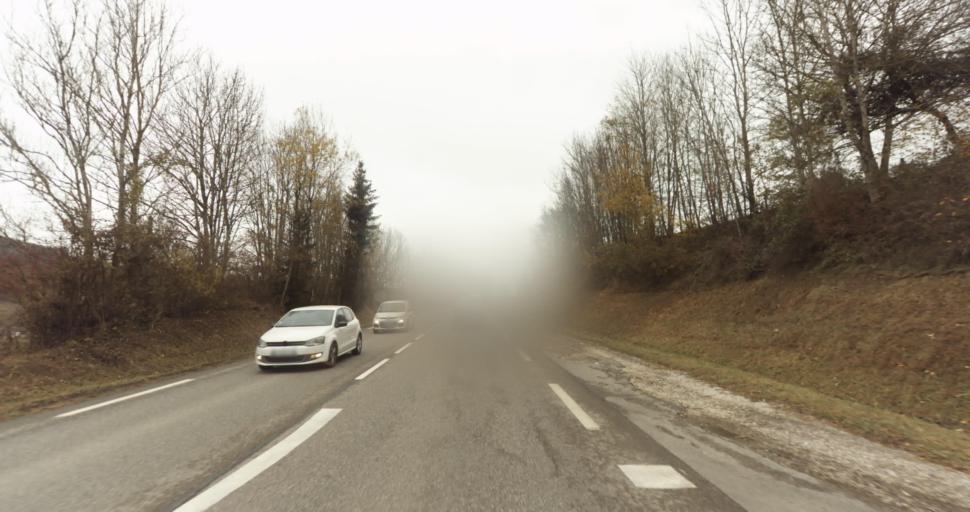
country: FR
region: Rhone-Alpes
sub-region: Departement de la Haute-Savoie
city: Evires
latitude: 46.0276
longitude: 6.2378
